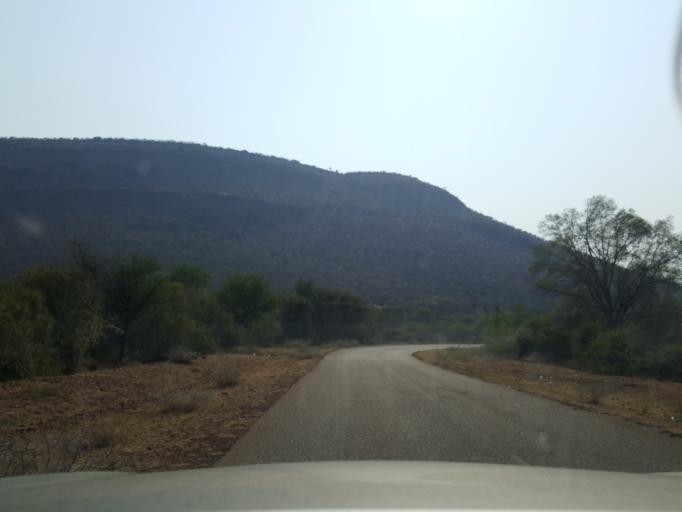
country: BW
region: South East
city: Lobatse
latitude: -25.3270
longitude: 25.7712
